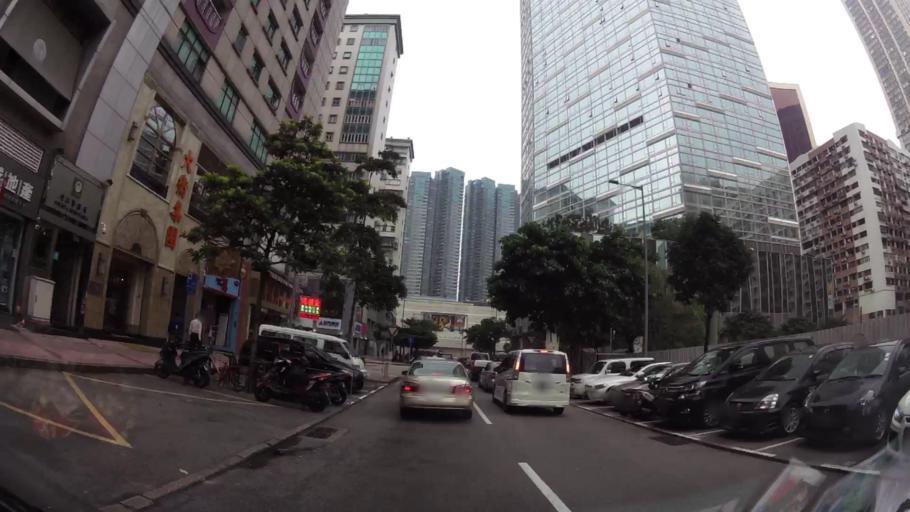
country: MO
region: Macau
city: Macau
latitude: 22.1868
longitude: 113.5504
